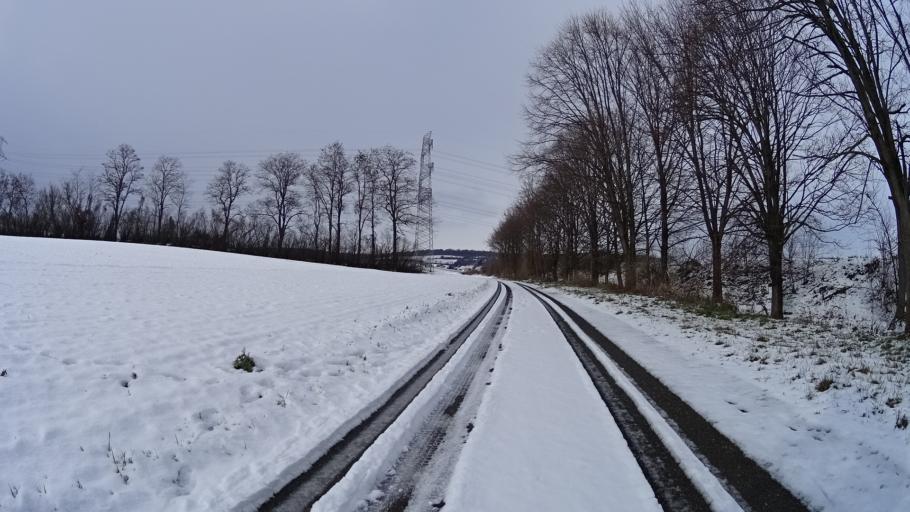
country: AT
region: Lower Austria
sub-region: Politischer Bezirk Korneuburg
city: Harmannsdorf
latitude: 48.3963
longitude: 16.3468
